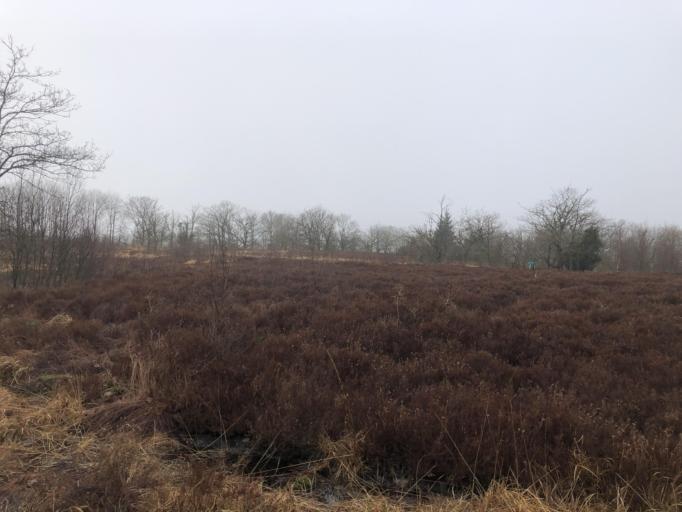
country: DK
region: Central Jutland
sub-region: Holstebro Kommune
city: Holstebro
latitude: 56.2469
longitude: 8.5139
